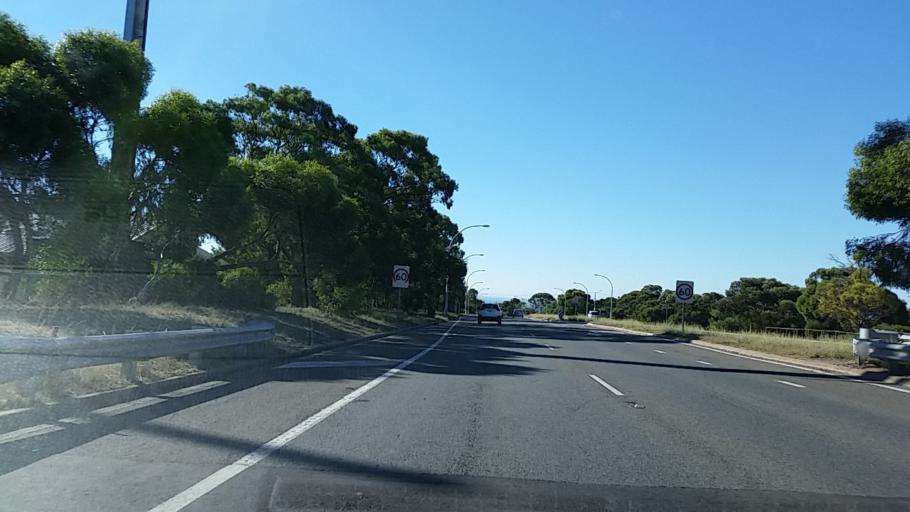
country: AU
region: South Australia
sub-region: Adelaide Hills
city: Seacliff
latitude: -35.0442
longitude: 138.5310
